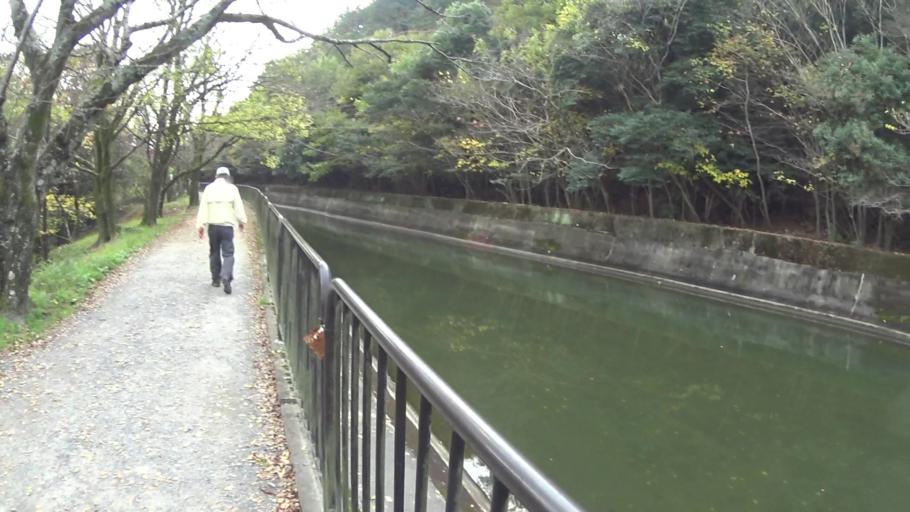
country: JP
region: Shiga Prefecture
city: Otsu-shi
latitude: 34.9943
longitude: 135.8135
